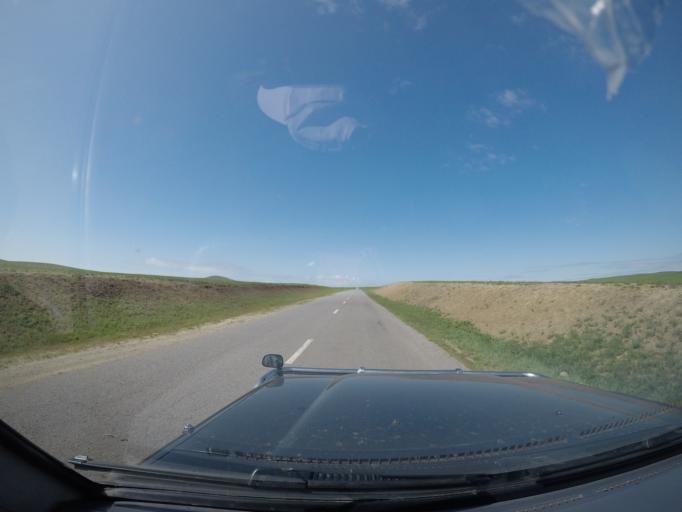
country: MN
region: Suhbaatar
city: Hanhohiy
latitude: 47.3563
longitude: 111.6974
